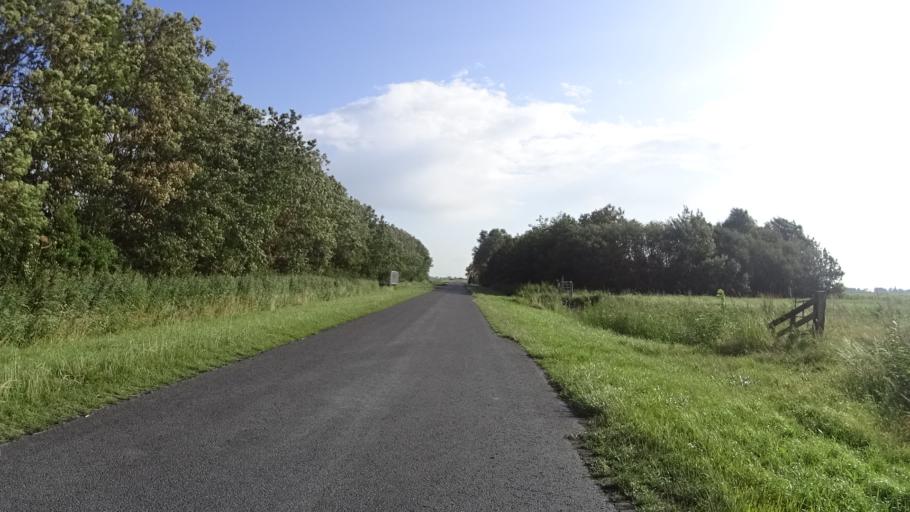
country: NL
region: Friesland
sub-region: Gemeente Harlingen
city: Harlingen
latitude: 53.1158
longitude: 5.4140
